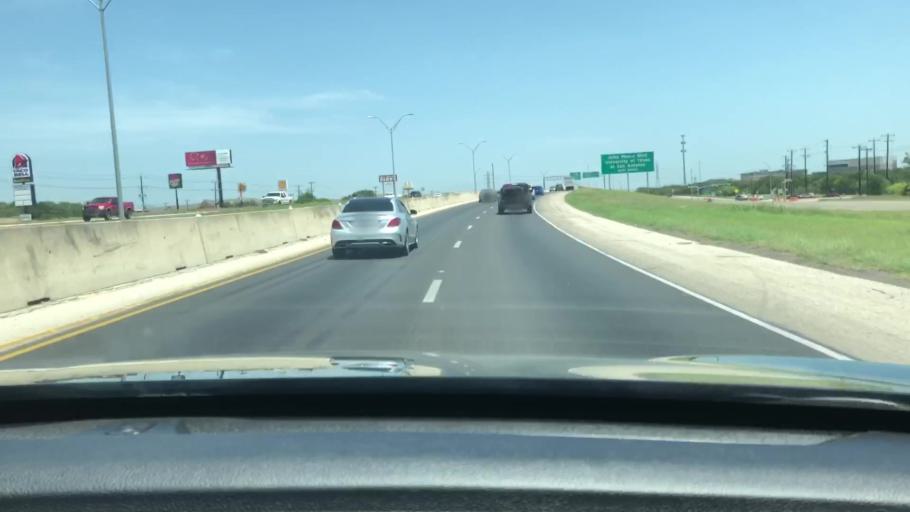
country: US
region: Texas
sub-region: Bexar County
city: Helotes
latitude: 29.5865
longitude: -98.6345
